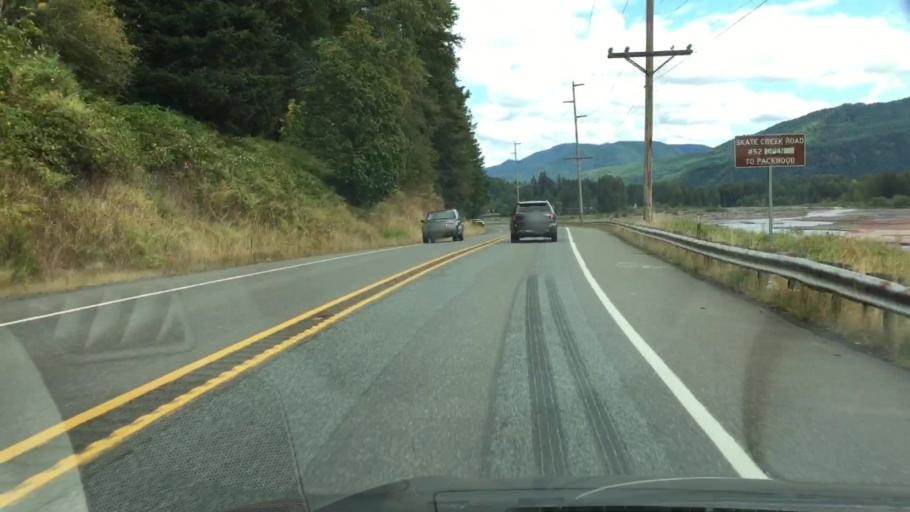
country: US
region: Washington
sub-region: Pierce County
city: Eatonville
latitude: 46.7708
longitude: -122.2086
